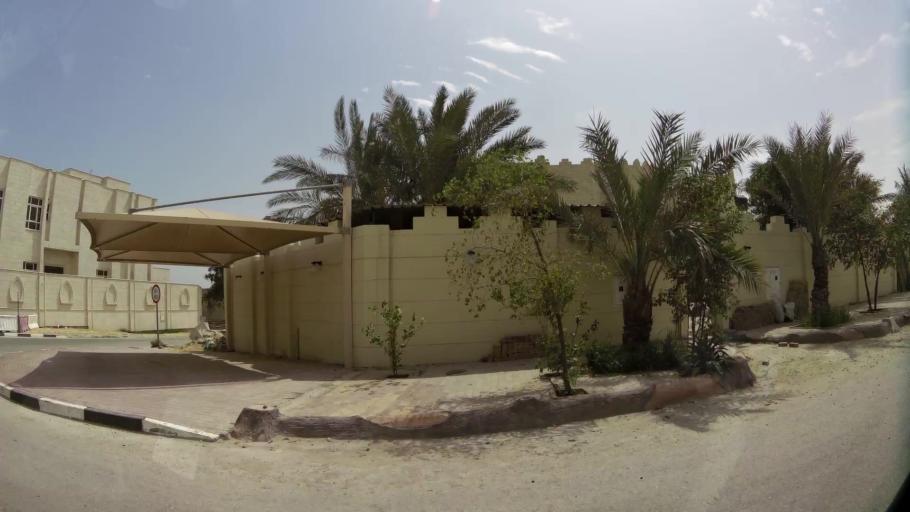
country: QA
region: Baladiyat ar Rayyan
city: Ar Rayyan
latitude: 25.3570
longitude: 51.4755
